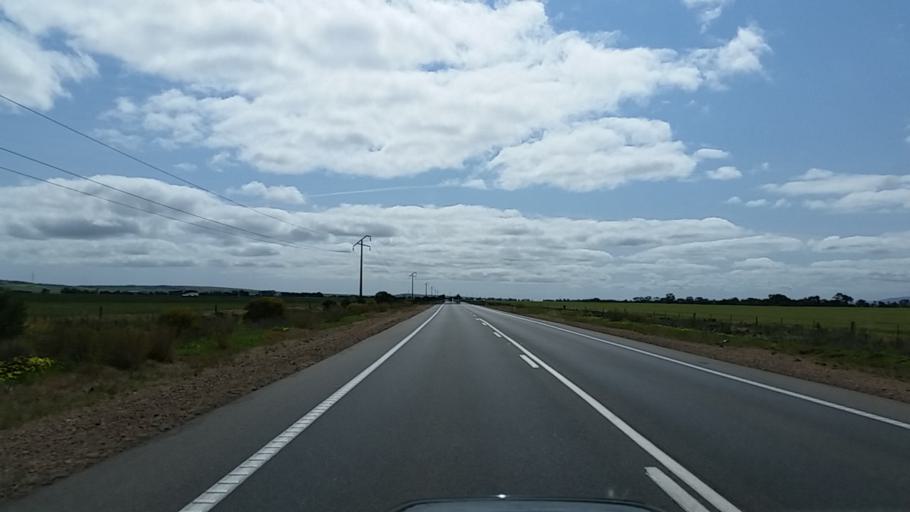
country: AU
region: South Australia
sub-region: Port Pirie City and Dists
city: Crystal Brook
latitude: -33.4888
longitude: 138.1783
